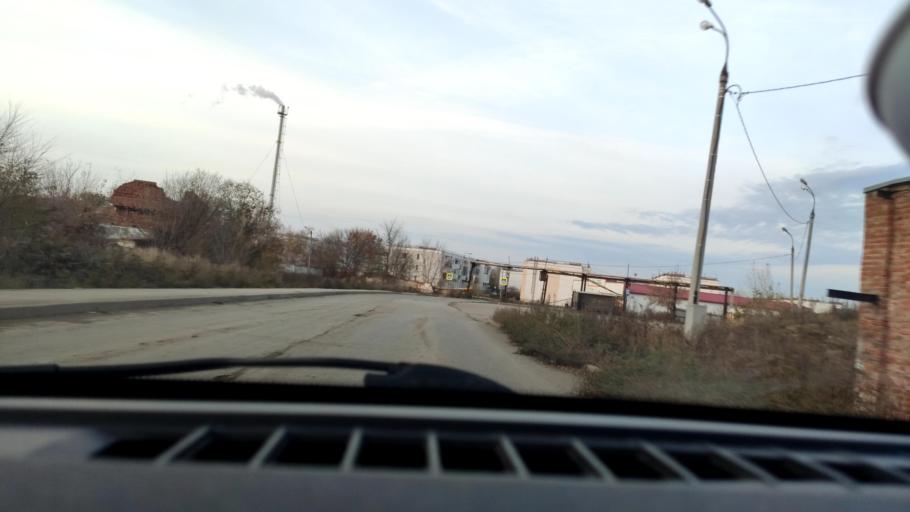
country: RU
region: Samara
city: Samara
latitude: 53.1481
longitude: 50.1406
